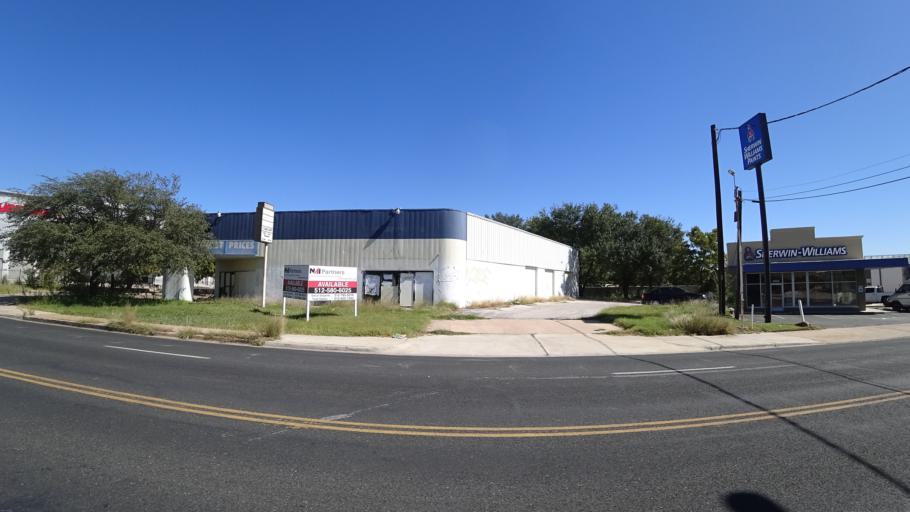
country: US
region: Texas
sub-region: Travis County
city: Austin
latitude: 30.3320
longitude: -97.7401
